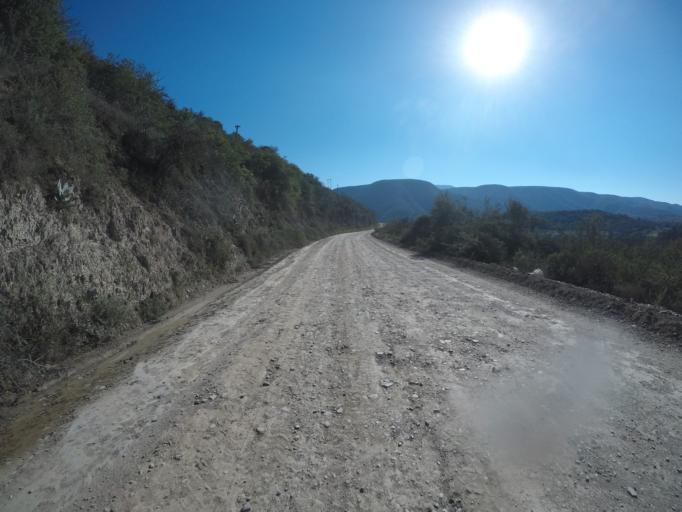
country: ZA
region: Eastern Cape
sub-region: Cacadu District Municipality
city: Kruisfontein
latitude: -33.6662
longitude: 24.5675
